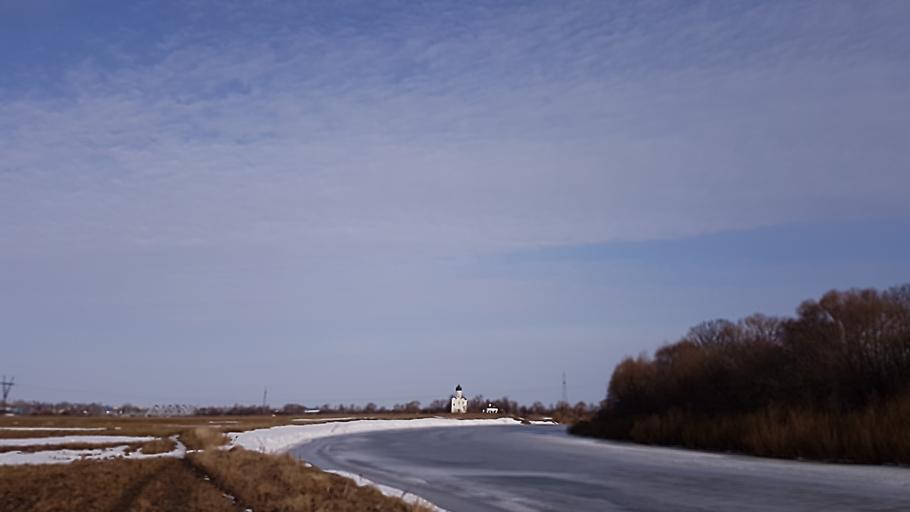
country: RU
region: Vladimir
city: Bogolyubovo
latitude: 56.1911
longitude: 40.5661
